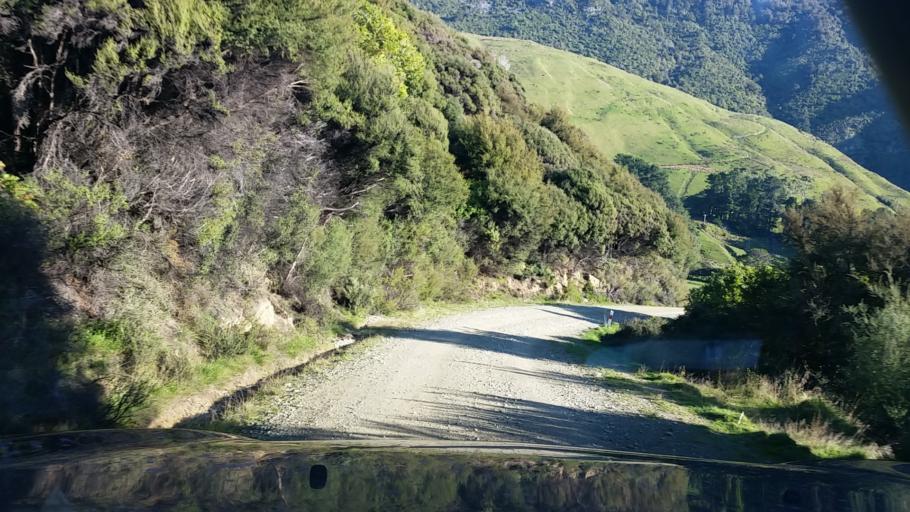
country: NZ
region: Marlborough
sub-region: Marlborough District
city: Picton
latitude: -41.0192
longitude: 174.1394
